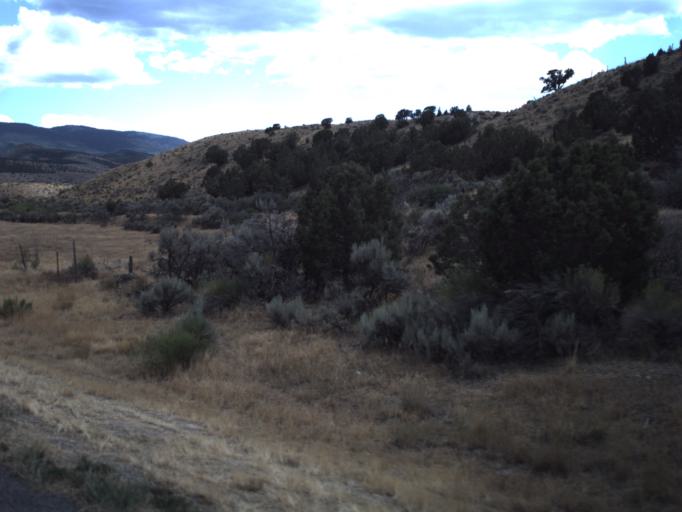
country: US
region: Utah
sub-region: Sanpete County
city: Centerfield
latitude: 39.1261
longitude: -111.7224
